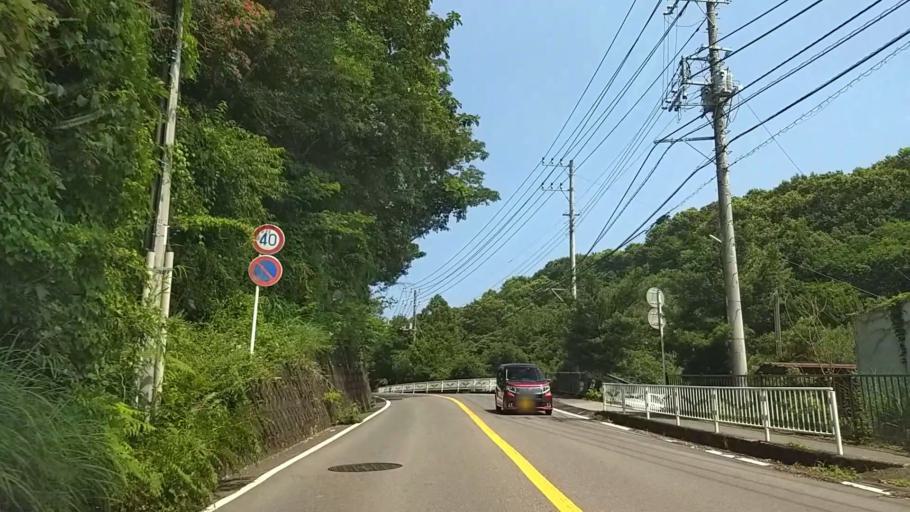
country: JP
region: Shizuoka
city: Ito
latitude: 34.9339
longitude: 139.0988
